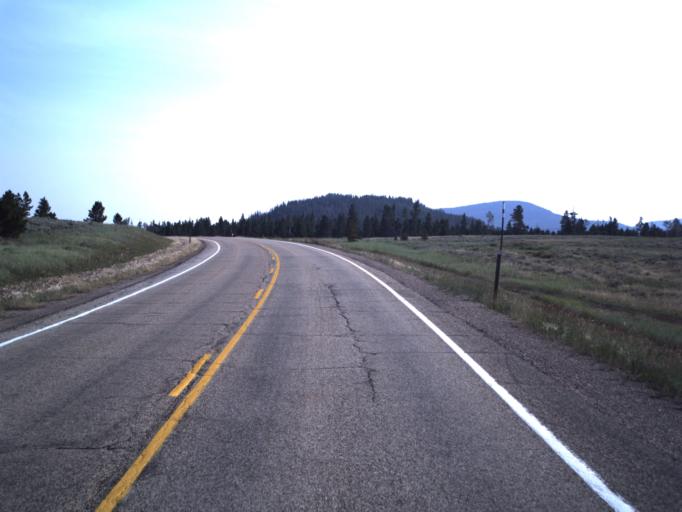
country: US
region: Utah
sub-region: Daggett County
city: Manila
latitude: 40.7953
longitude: -109.4667
